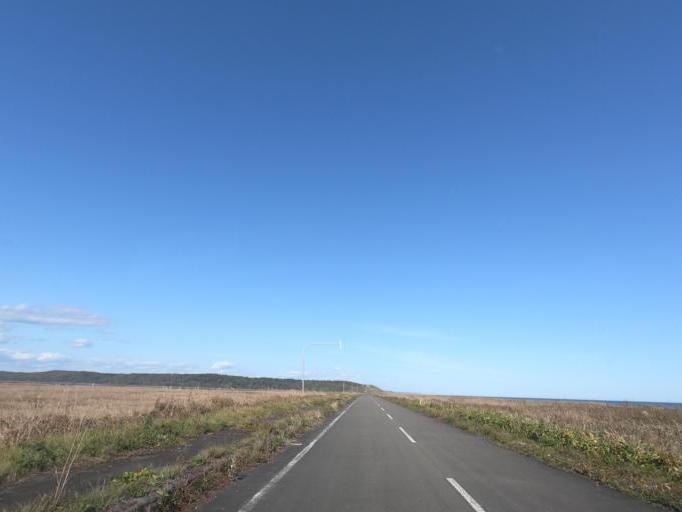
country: JP
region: Hokkaido
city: Obihiro
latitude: 42.5906
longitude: 143.5403
